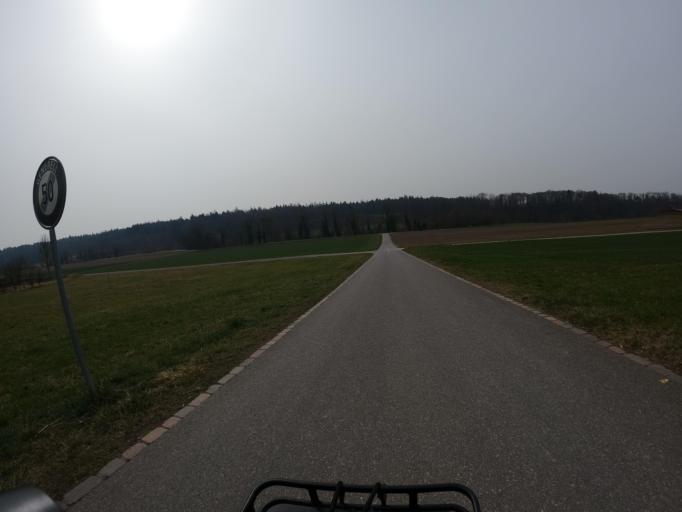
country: CH
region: Aargau
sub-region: Bezirk Lenzburg
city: Niederlenz
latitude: 47.4115
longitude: 8.1914
